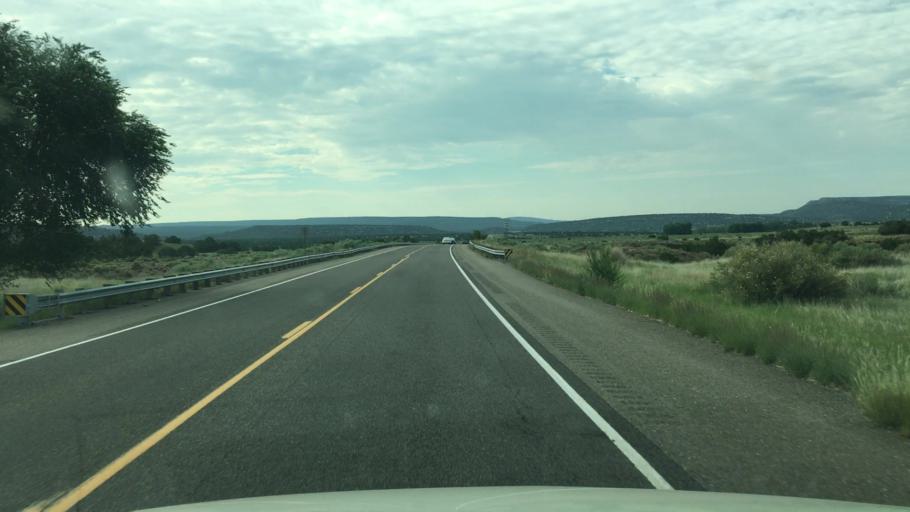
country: US
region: New Mexico
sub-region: Santa Fe County
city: Eldorado at Santa Fe
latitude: 35.4136
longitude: -105.8681
